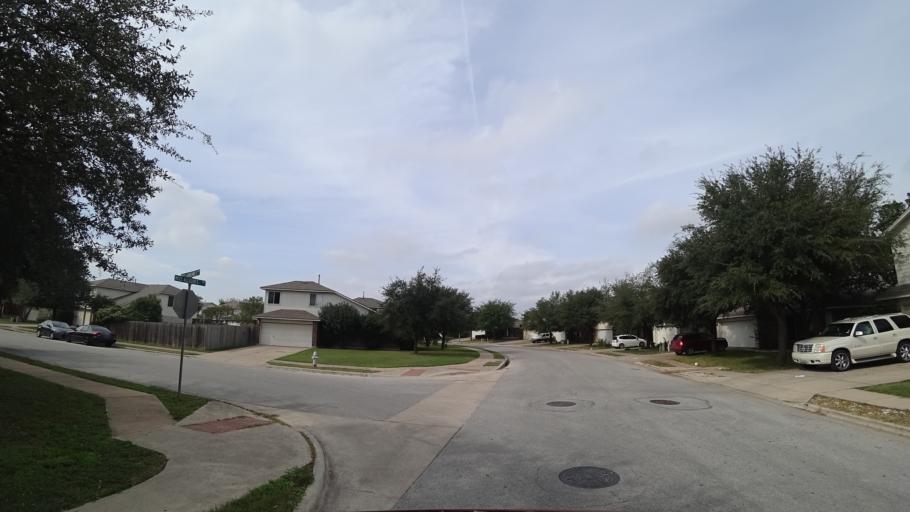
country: US
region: Texas
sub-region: Travis County
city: Windemere
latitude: 30.4485
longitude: -97.6582
